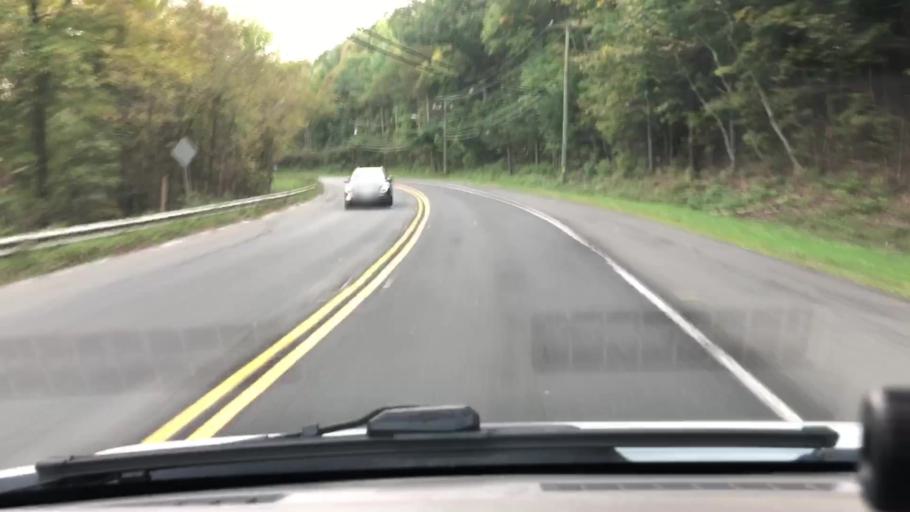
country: US
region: Massachusetts
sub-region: Berkshire County
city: Dalton
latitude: 42.4820
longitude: -73.2031
